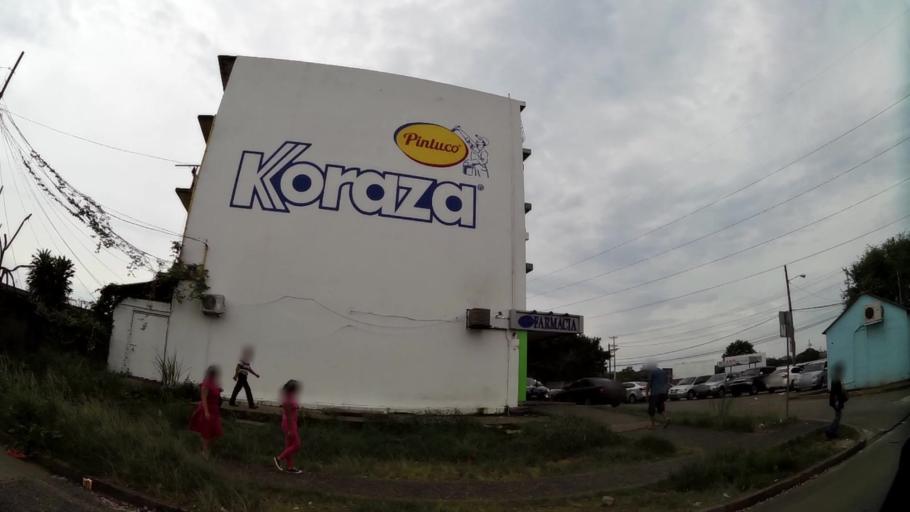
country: PA
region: Panama
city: San Miguelito
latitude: 9.0333
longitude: -79.4734
